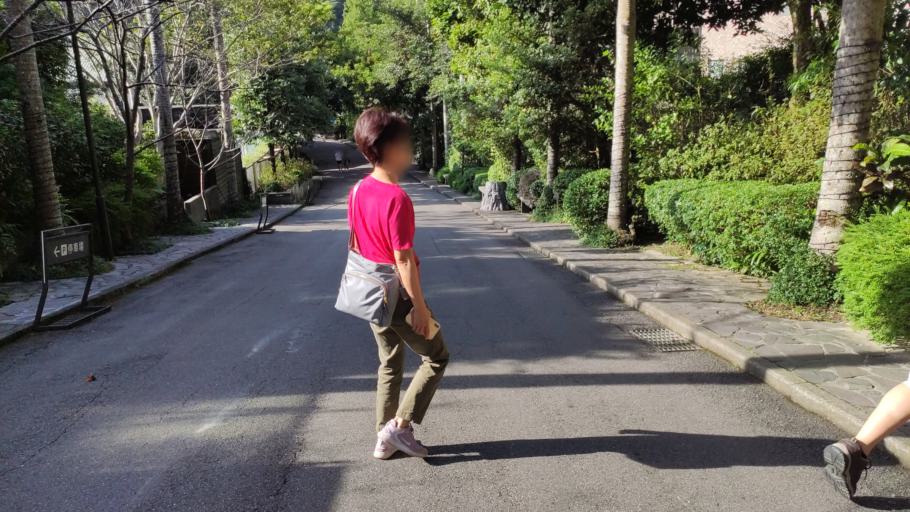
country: TW
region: Taiwan
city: Daxi
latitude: 24.8714
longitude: 121.4075
